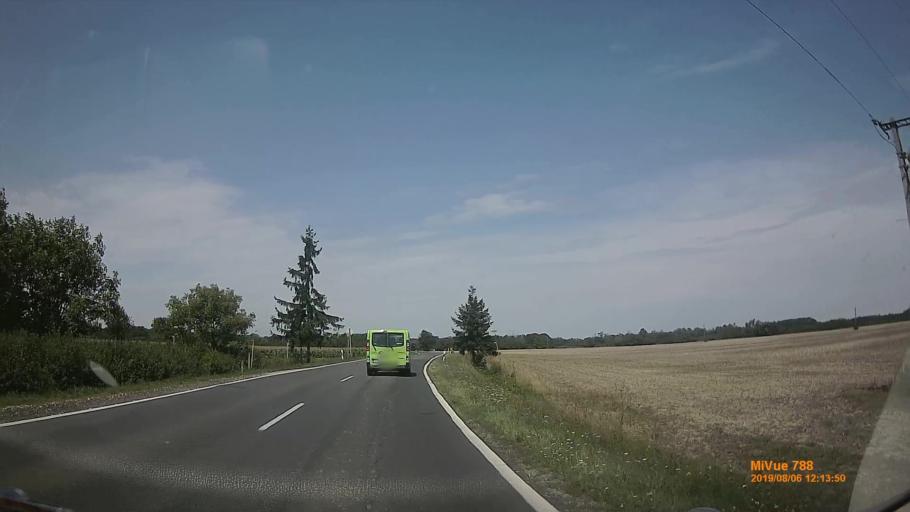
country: HU
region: Vas
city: Vasvar
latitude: 47.1344
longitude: 16.8368
